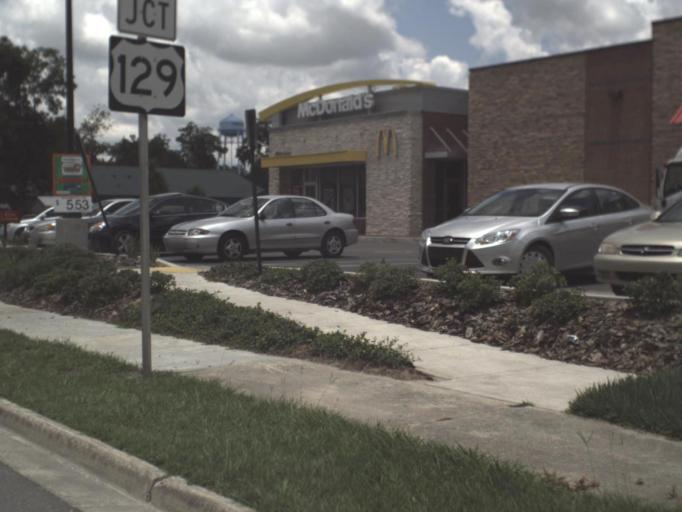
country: US
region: Florida
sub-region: Gilchrist County
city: Trenton
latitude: 29.6134
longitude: -82.8164
